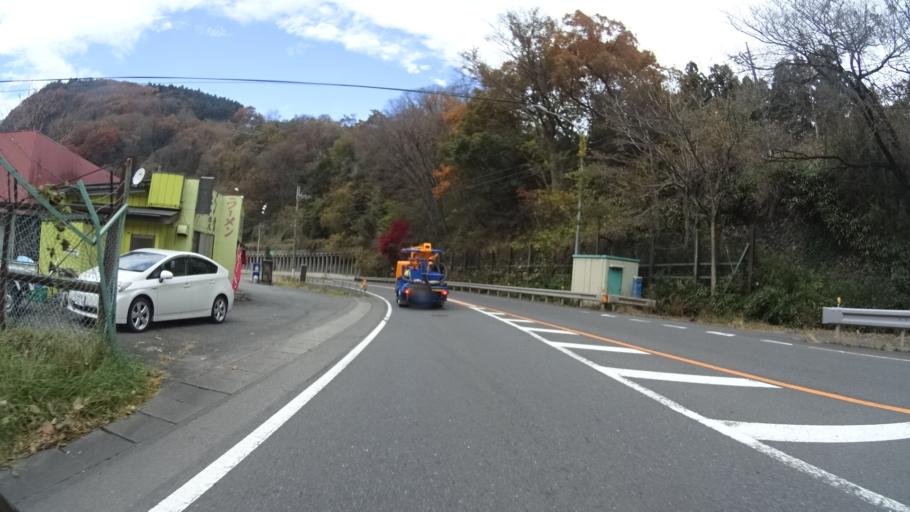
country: JP
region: Gunma
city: Numata
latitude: 36.5855
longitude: 139.0548
